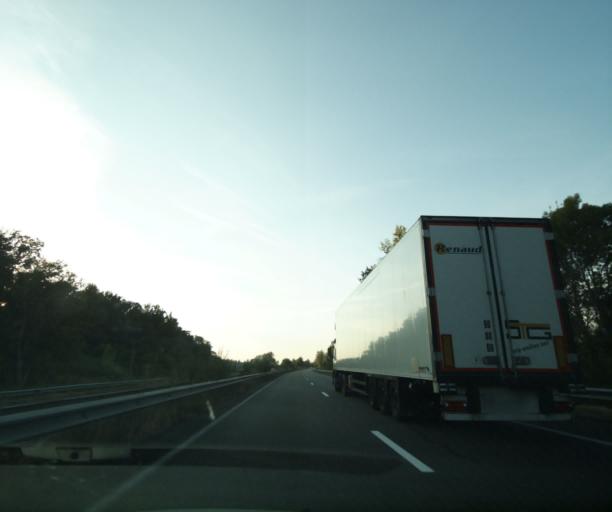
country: FR
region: Aquitaine
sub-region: Departement du Lot-et-Garonne
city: Layrac
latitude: 44.1315
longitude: 0.6812
